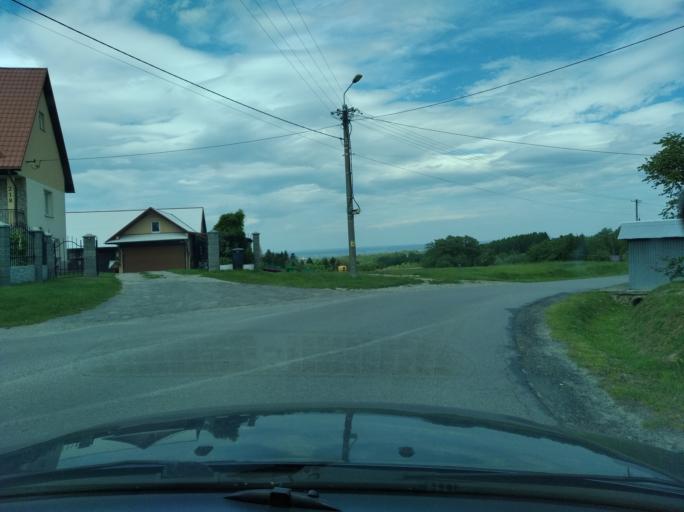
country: PL
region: Subcarpathian Voivodeship
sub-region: Powiat ropczycko-sedziszowski
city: Ropczyce
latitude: 50.0245
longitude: 21.6044
